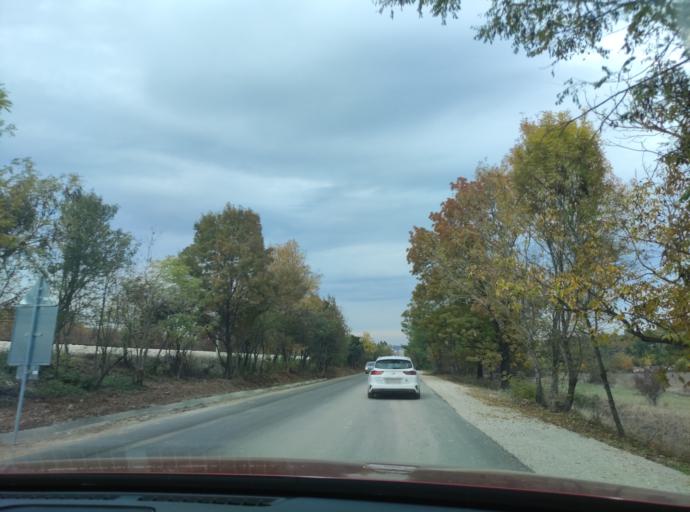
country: BG
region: Montana
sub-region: Obshtina Montana
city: Montana
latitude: 43.3878
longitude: 23.2428
